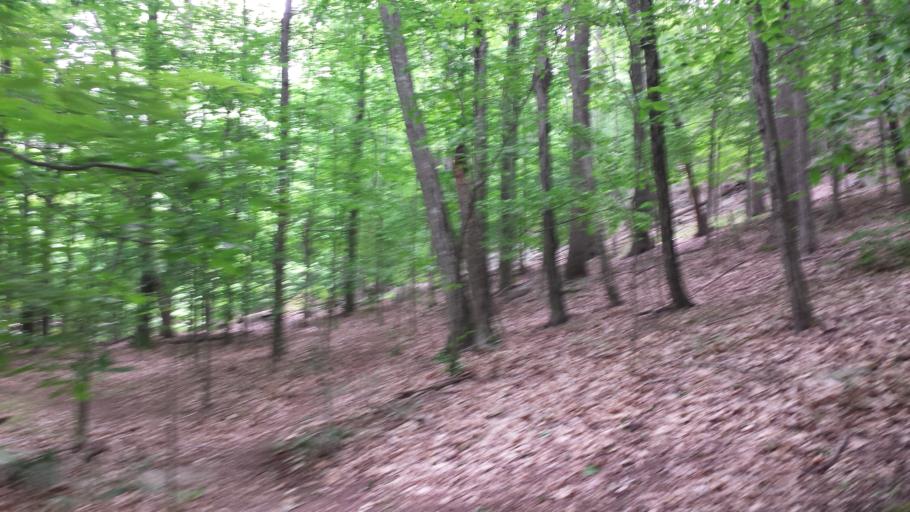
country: US
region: New York
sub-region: Putnam County
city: Peach Lake
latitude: 41.3131
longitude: -73.5680
